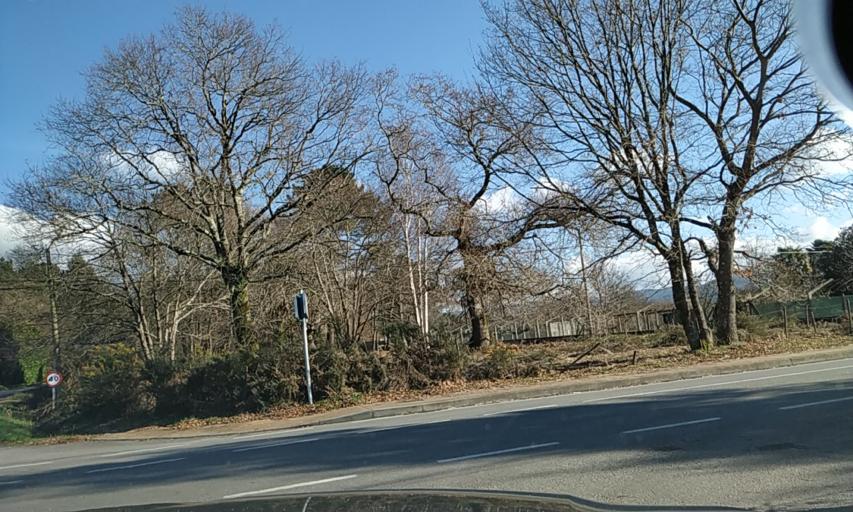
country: ES
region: Galicia
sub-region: Provincia da Coruna
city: Ribeira
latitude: 42.7136
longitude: -8.4459
